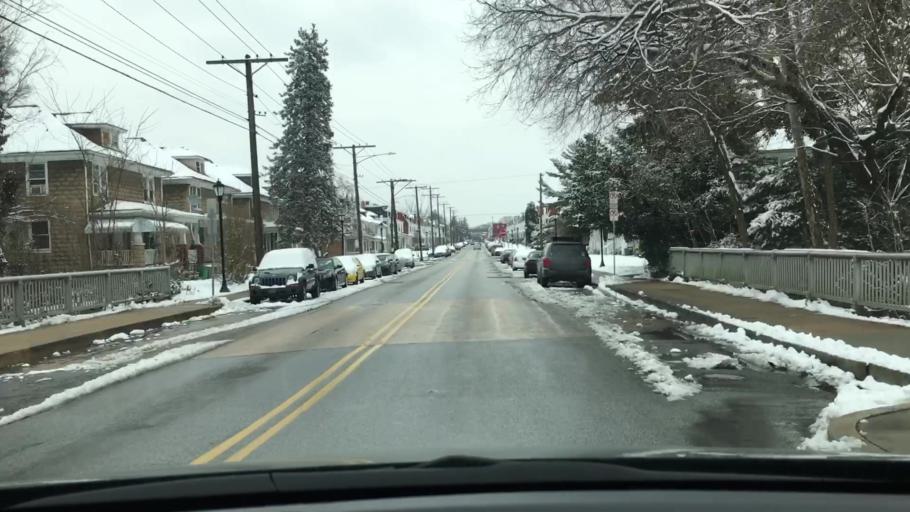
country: US
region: Pennsylvania
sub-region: York County
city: Grantley
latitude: 39.9495
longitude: -76.7319
